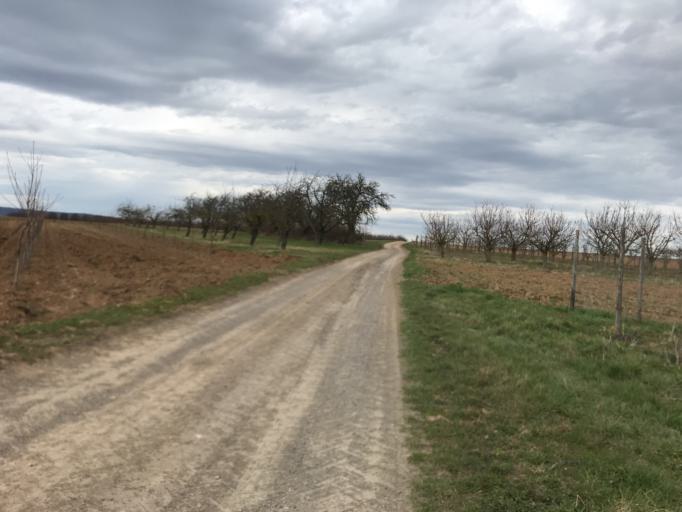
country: DE
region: Rheinland-Pfalz
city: Wackernheim
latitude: 49.9538
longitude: 8.1034
